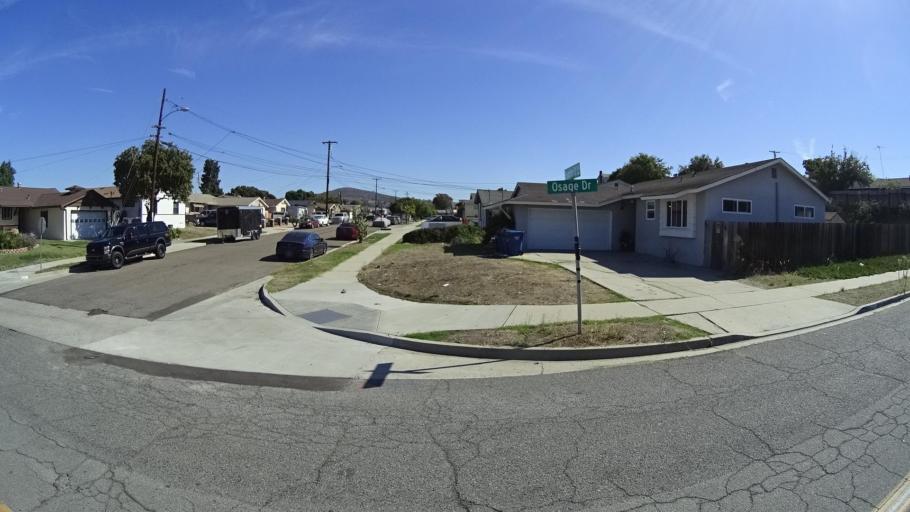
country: US
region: California
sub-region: San Diego County
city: Lemon Grove
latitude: 32.7197
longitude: -117.0231
